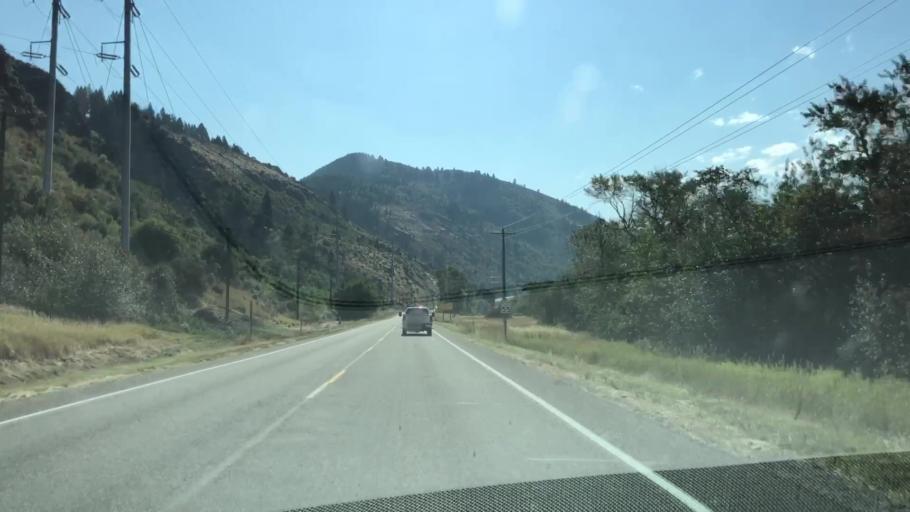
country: US
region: Idaho
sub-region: Teton County
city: Victor
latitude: 43.3488
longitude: -111.2143
